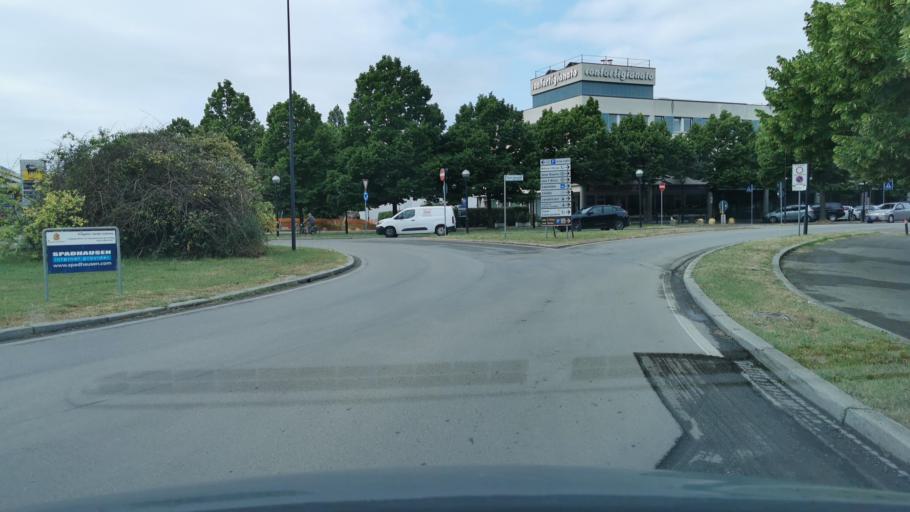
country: IT
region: Emilia-Romagna
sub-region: Provincia di Ravenna
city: Ravenna
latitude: 44.4033
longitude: 12.1967
